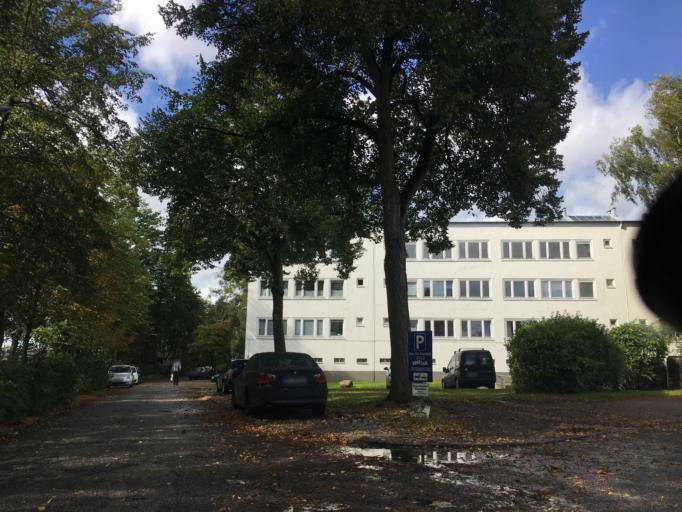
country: DE
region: Hamburg
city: Eidelstedt
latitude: 53.5707
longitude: 9.8979
